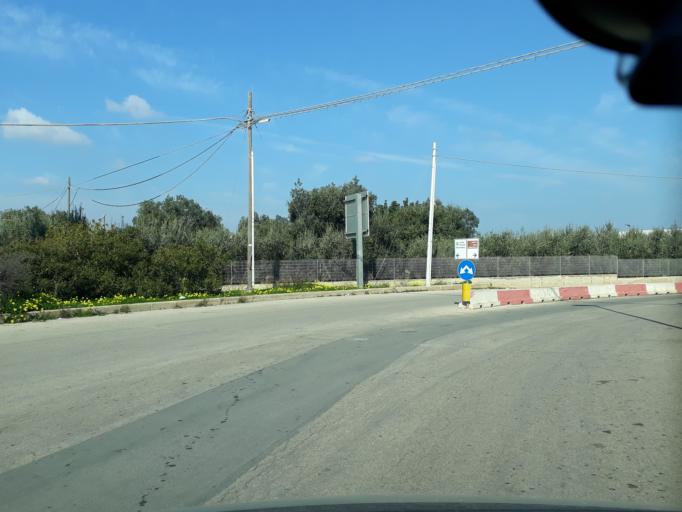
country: IT
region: Apulia
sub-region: Provincia di Brindisi
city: Fasano
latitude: 40.8266
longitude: 17.3833
